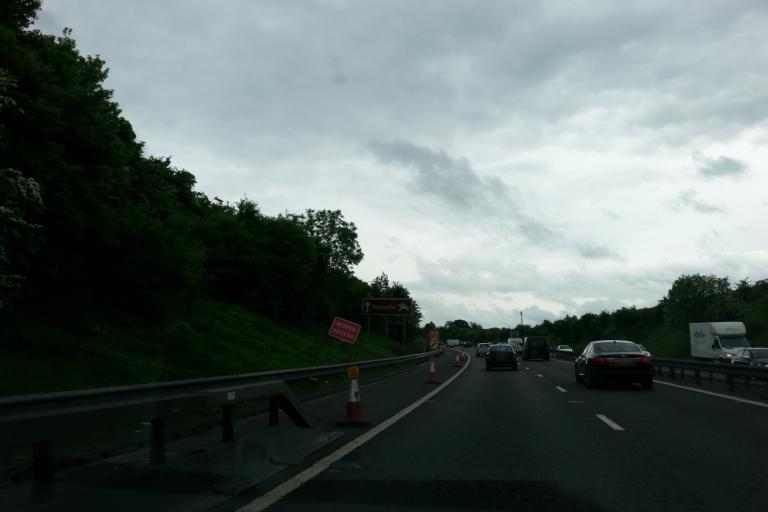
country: GB
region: England
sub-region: Doncaster
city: Bentley
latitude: 53.5072
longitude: -1.1772
